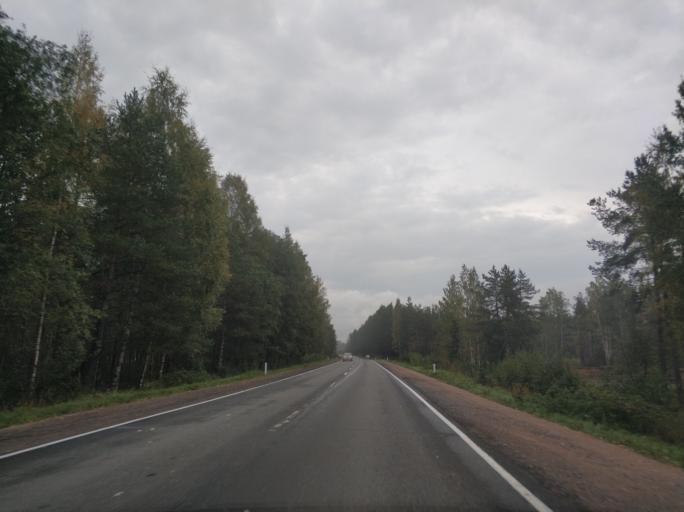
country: RU
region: Leningrad
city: Borisova Griva
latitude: 60.0886
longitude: 30.8660
